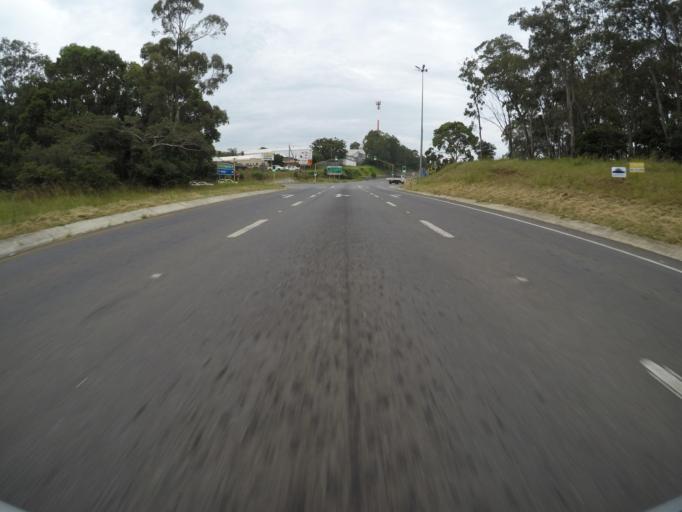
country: ZA
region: Eastern Cape
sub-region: Buffalo City Metropolitan Municipality
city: East London
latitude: -32.9382
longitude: 27.9506
